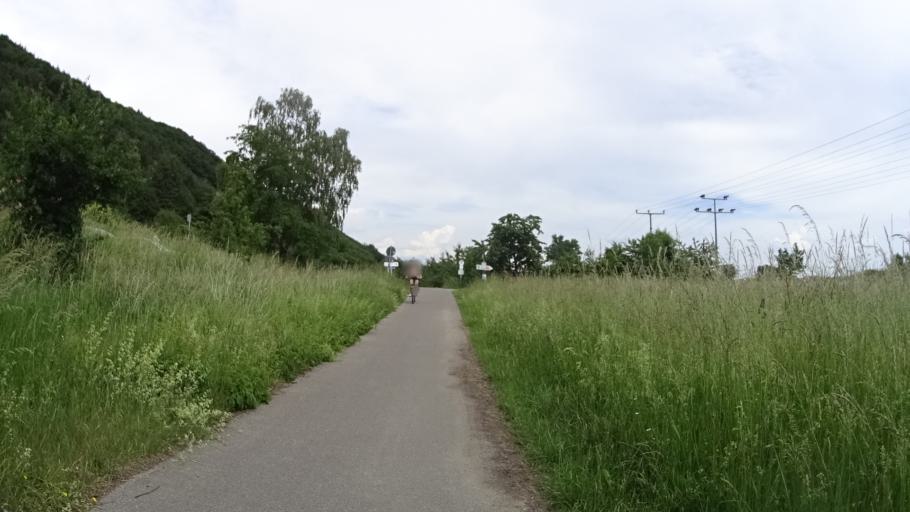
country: DE
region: Bavaria
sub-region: Upper Palatinate
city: Donaustauf
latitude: 49.0232
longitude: 12.2529
